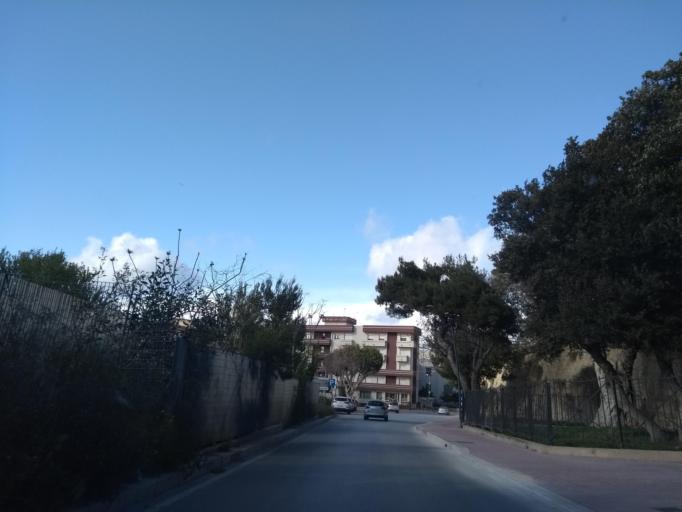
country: IT
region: Sicily
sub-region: Trapani
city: Marsala
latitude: 37.8037
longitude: 12.4335
